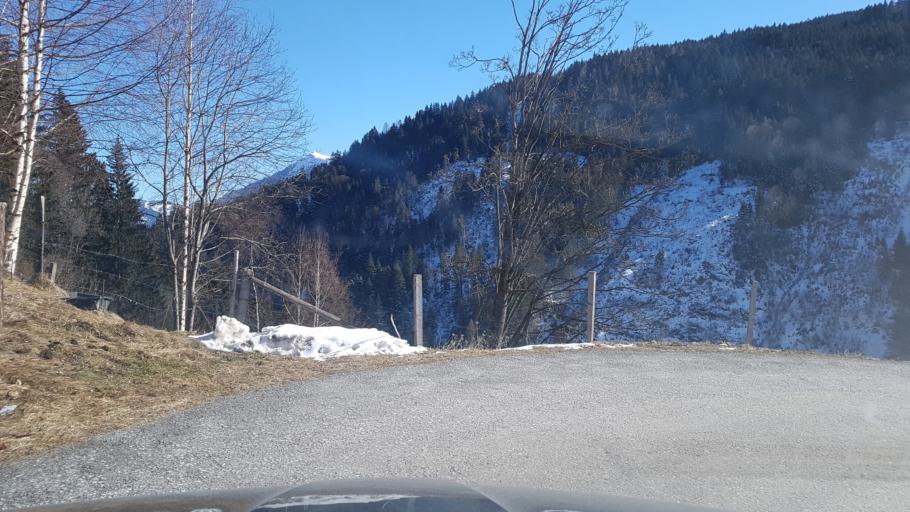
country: AT
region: Salzburg
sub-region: Politischer Bezirk Zell am See
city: Lend
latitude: 47.3176
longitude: 13.0505
